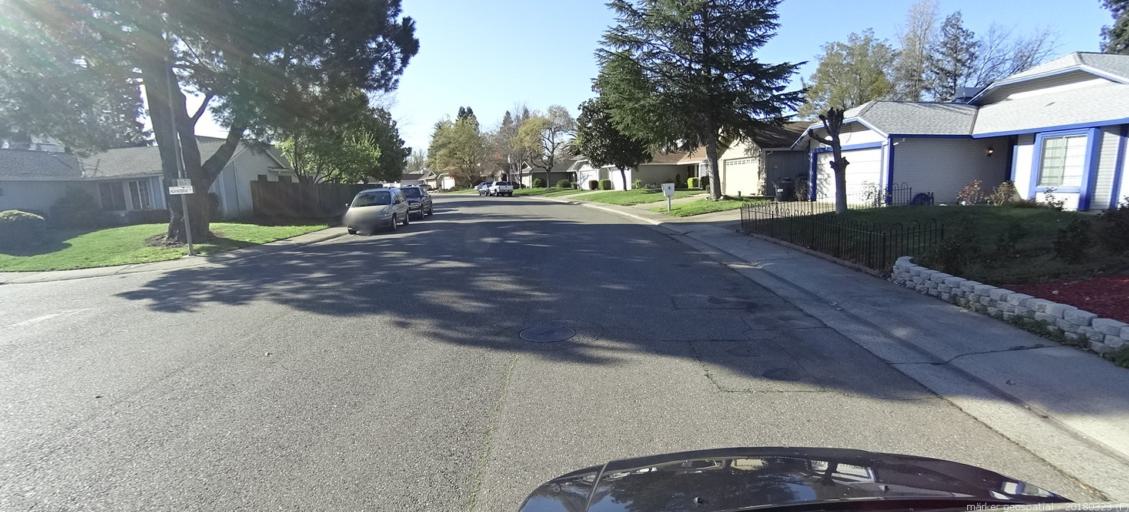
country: US
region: California
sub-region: Sacramento County
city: Antelope
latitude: 38.7035
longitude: -121.3543
